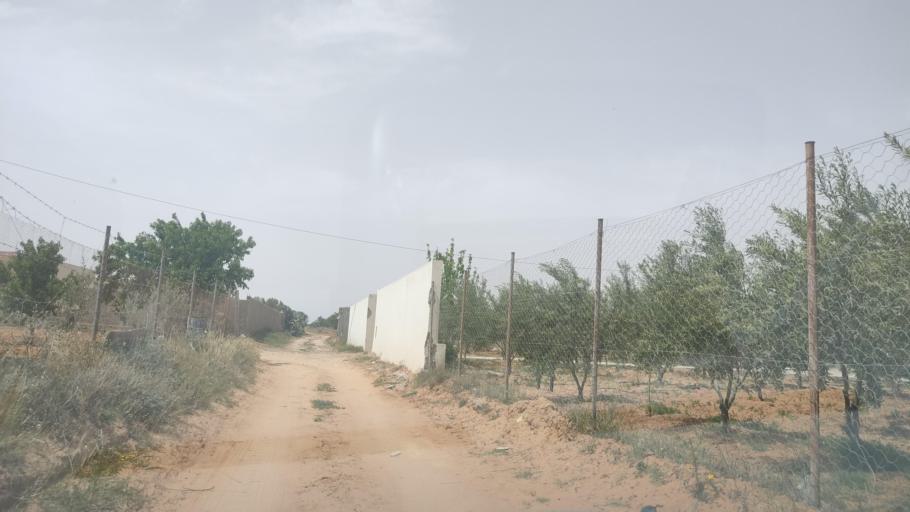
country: TN
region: Safaqis
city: Sfax
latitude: 34.8445
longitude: 10.5880
